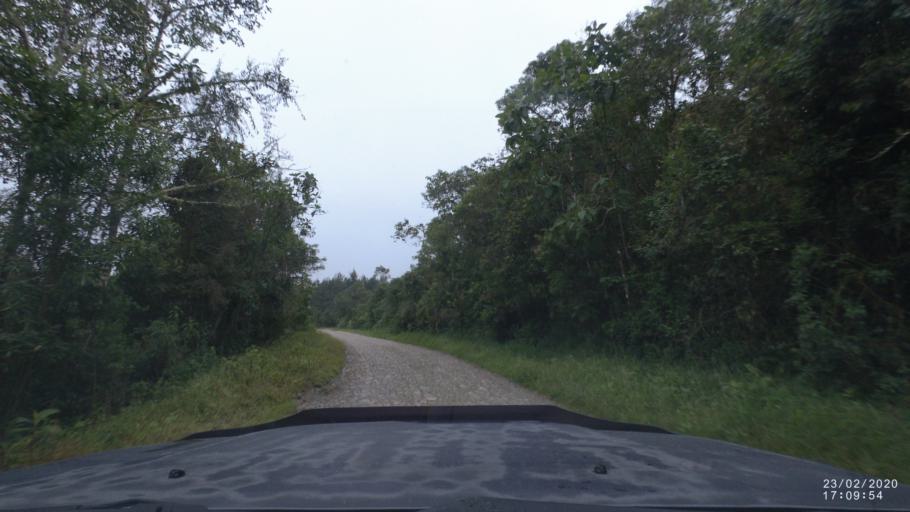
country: BO
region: Cochabamba
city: Colomi
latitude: -17.1314
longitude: -65.9504
